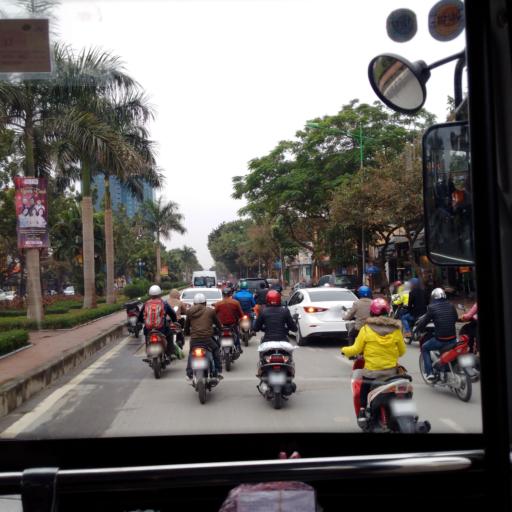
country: VN
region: Ha Noi
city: Cau Giay
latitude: 21.0464
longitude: 105.8050
